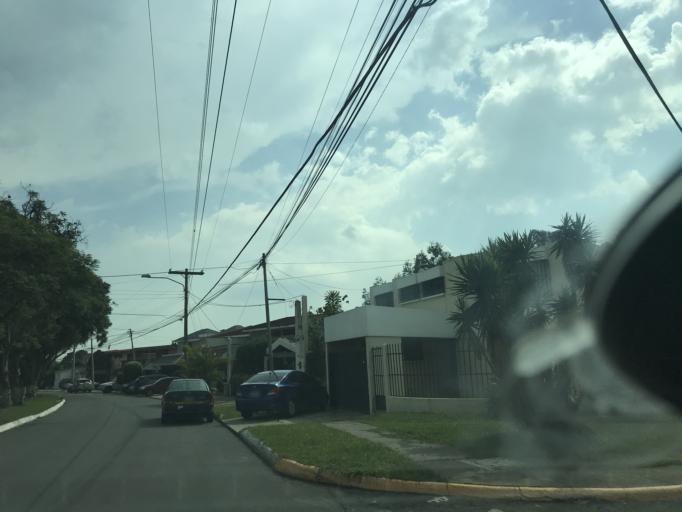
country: GT
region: Guatemala
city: Santa Catarina Pinula
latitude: 14.5837
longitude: -90.5506
